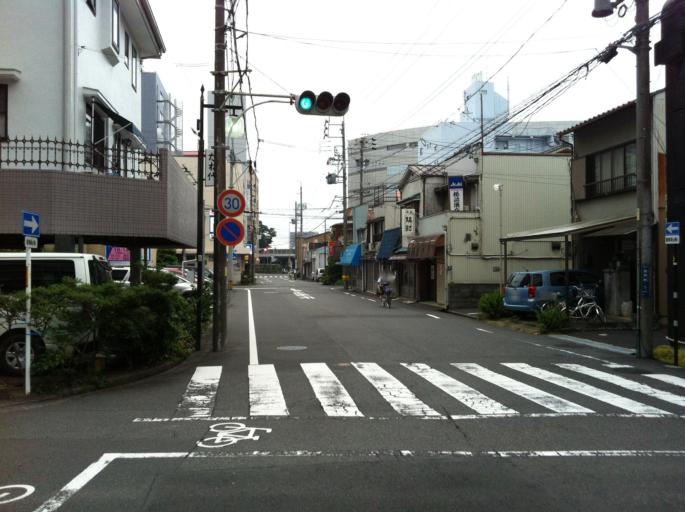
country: JP
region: Shizuoka
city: Shizuoka-shi
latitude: 34.9699
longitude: 138.3821
